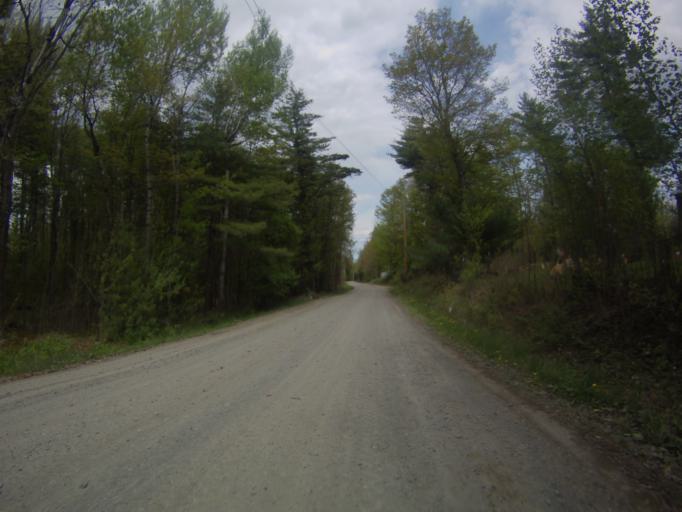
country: US
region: New York
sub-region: Essex County
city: Ticonderoga
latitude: 43.9177
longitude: -73.5088
